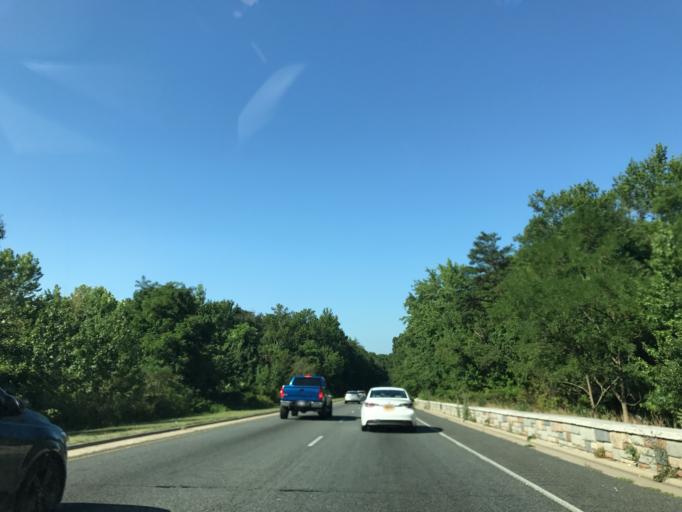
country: US
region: Maryland
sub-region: Anne Arundel County
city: Maryland City
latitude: 39.0883
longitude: -76.8111
